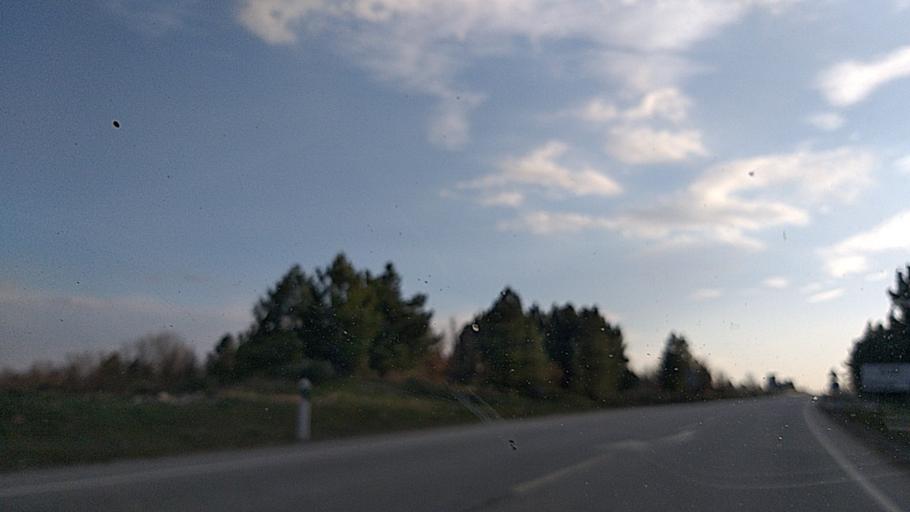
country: ES
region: Castille and Leon
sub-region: Provincia de Salamanca
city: Fuentes de Onoro
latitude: 40.6050
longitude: -6.9842
